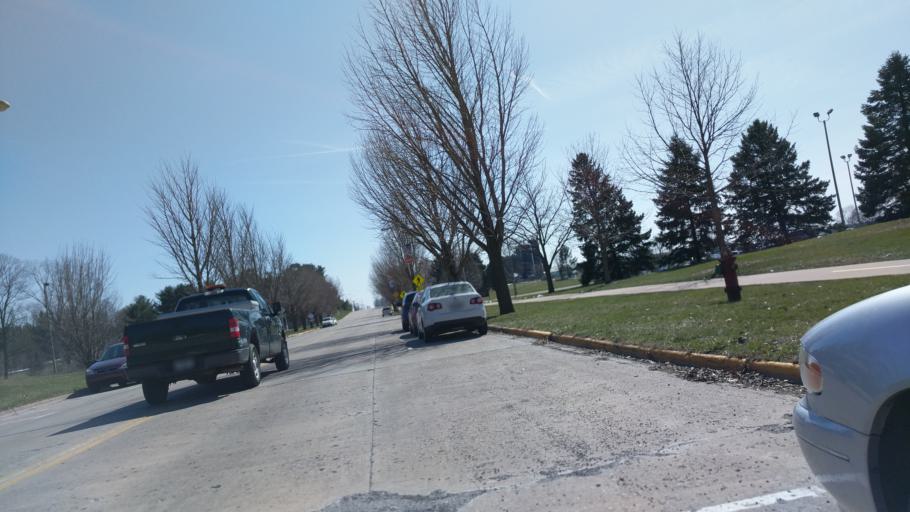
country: US
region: Illinois
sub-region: Champaign County
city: Urbana
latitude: 40.0928
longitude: -88.2189
